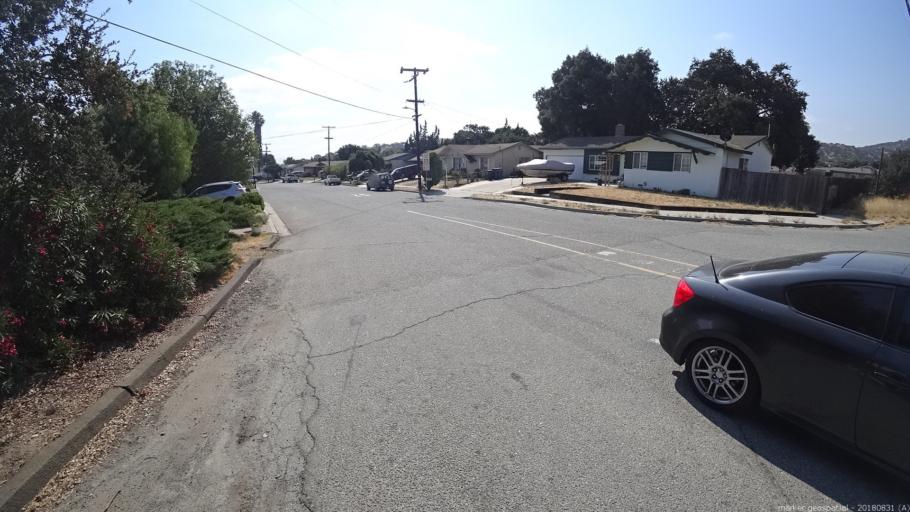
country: US
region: California
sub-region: Monterey County
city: King City
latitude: 36.1840
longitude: -121.1504
